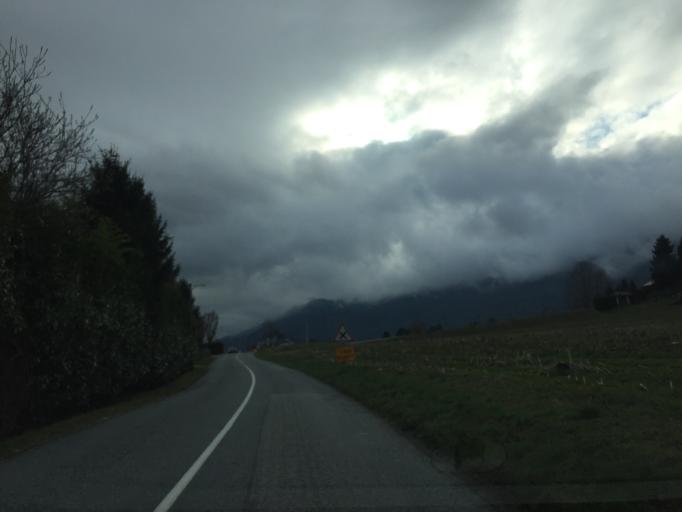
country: FR
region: Rhone-Alpes
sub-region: Departement de la Savoie
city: Vimines
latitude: 45.5453
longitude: 5.8683
